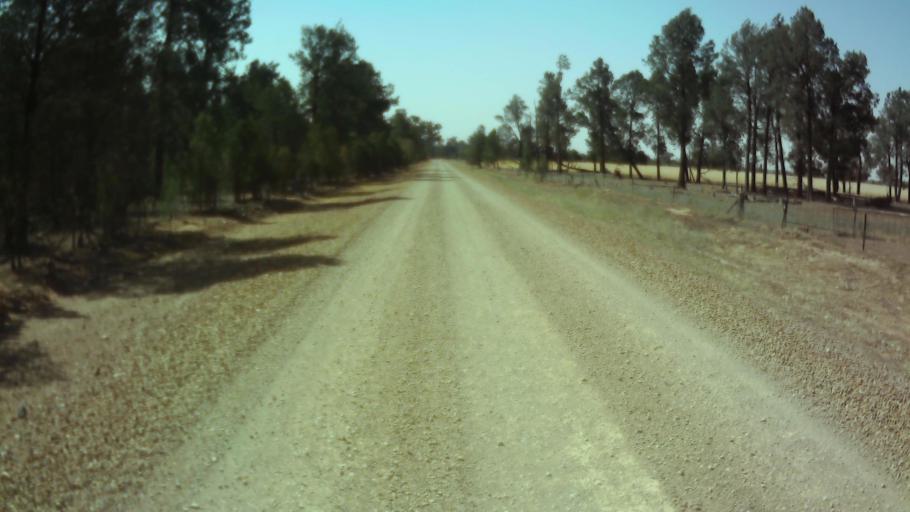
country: AU
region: New South Wales
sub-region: Weddin
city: Grenfell
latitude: -33.9535
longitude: 147.9304
